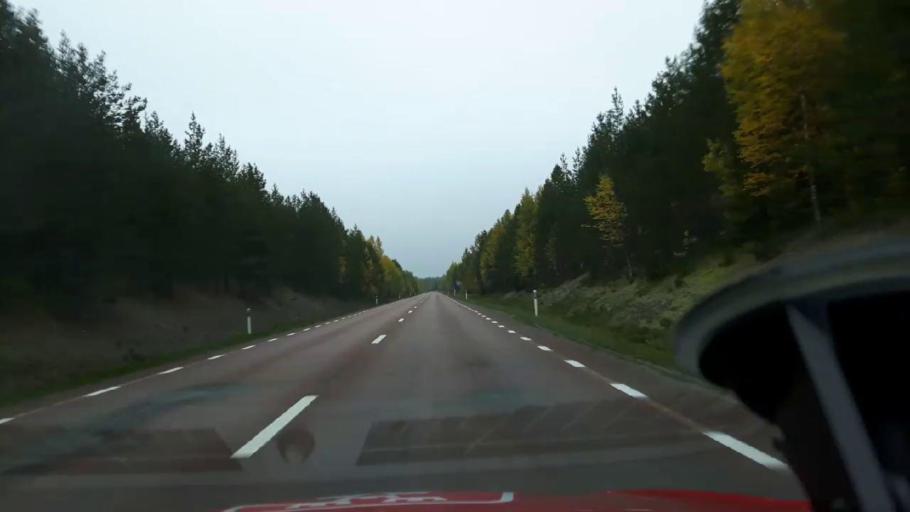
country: SE
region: Jaemtland
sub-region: Bergs Kommun
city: Hoverberg
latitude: 62.6284
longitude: 14.3695
